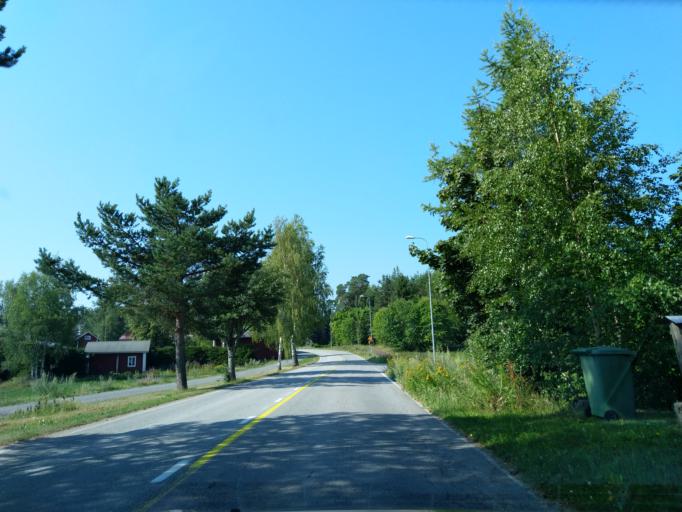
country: FI
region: Satakunta
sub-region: Pori
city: Pomarkku
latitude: 61.6913
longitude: 22.0058
